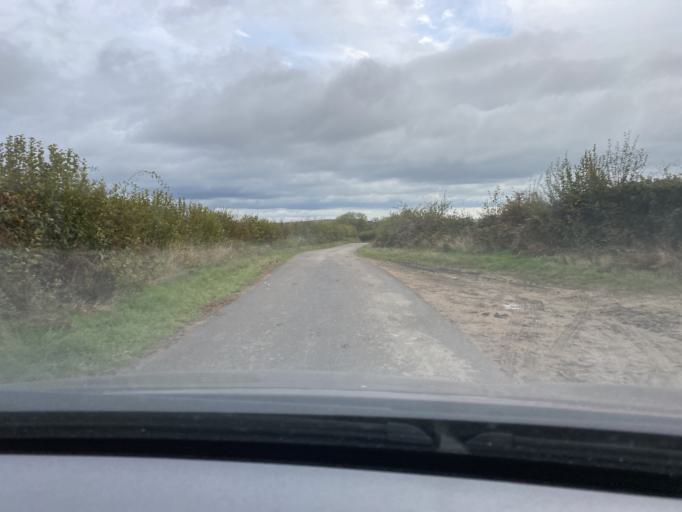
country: FR
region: Bourgogne
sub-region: Departement de la Cote-d'Or
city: Saulieu
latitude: 47.2857
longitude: 4.2205
